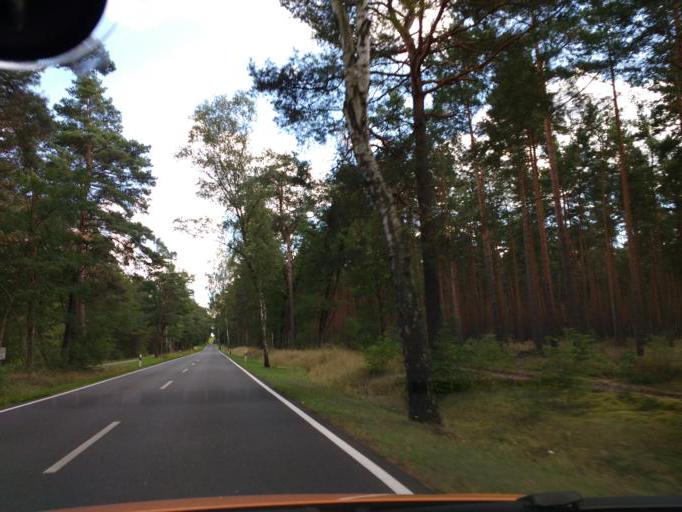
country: DE
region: Brandenburg
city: Wendisch Rietz
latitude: 52.2110
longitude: 13.9963
